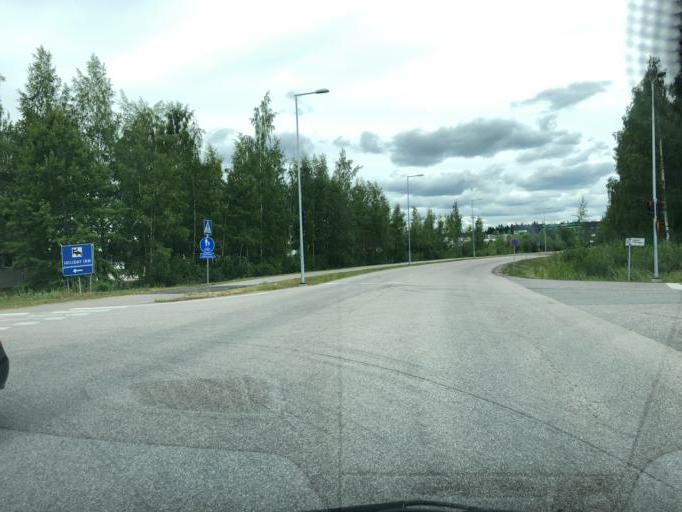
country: FI
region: Uusimaa
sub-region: Helsinki
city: Vantaa
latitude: 60.2971
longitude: 24.9730
